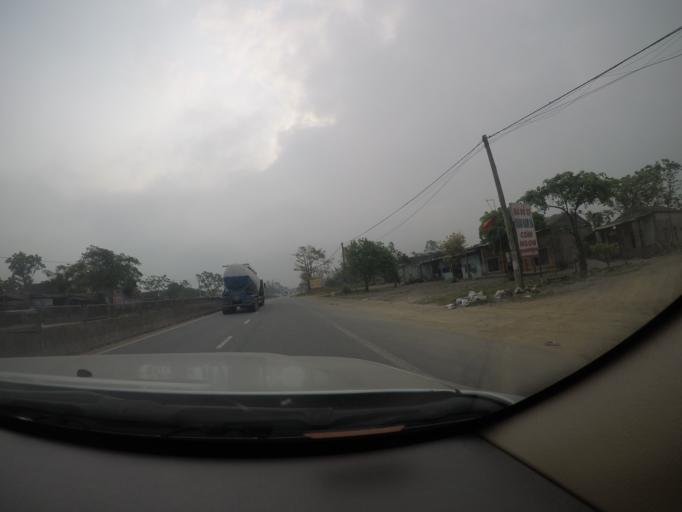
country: VN
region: Ha Tinh
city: Cam Xuyen
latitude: 18.2040
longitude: 106.1403
